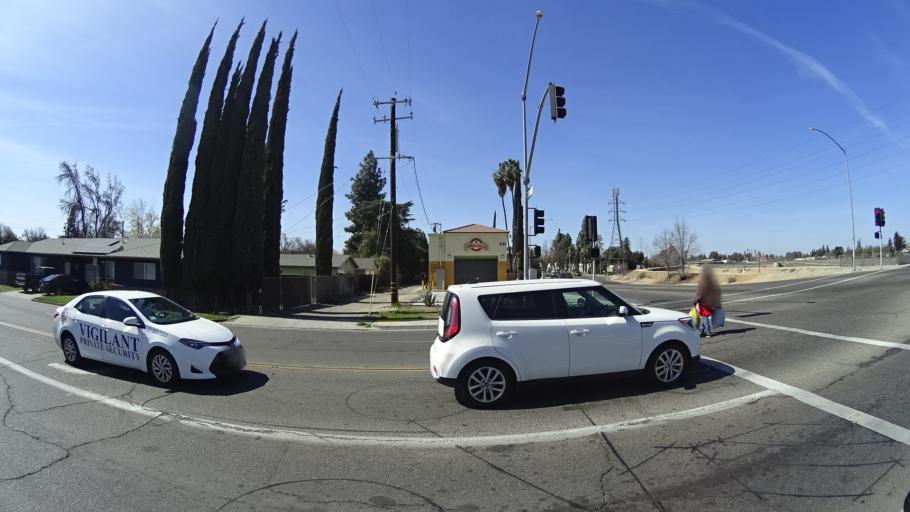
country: US
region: California
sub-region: Fresno County
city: Fresno
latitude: 36.7863
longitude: -119.8085
